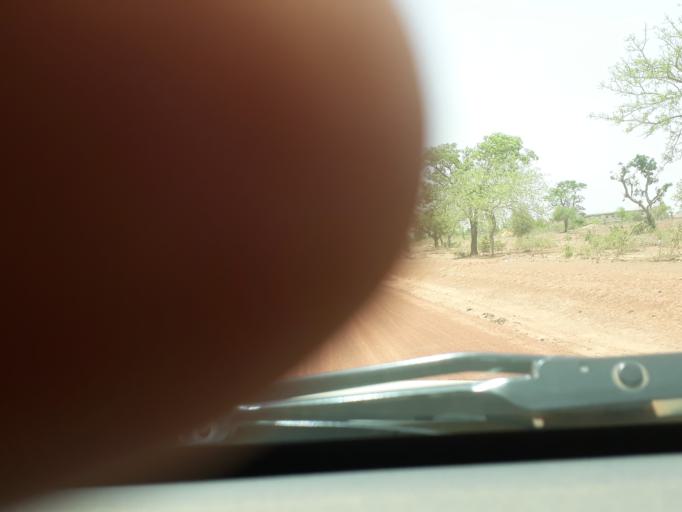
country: BF
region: Plateau-Central
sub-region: Province d'Oubritenga
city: Ziniare
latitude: 12.5798
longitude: -1.3355
